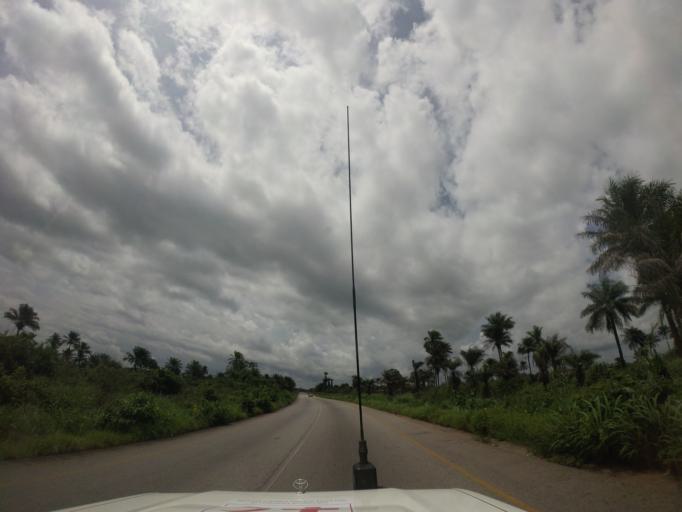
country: SL
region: Southern Province
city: Rotifunk
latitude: 8.4567
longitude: -12.6631
